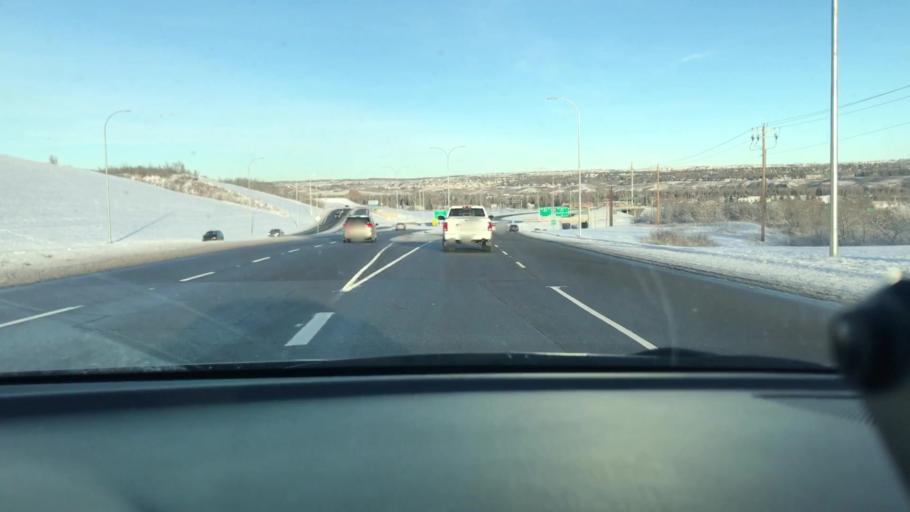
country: CA
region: Alberta
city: Calgary
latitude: 51.0748
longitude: -114.1861
